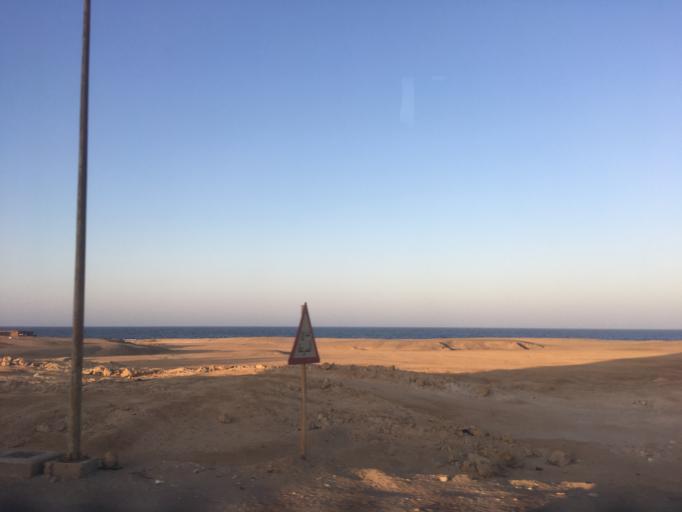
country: EG
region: Red Sea
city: Al Qusayr
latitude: 26.1493
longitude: 34.2508
